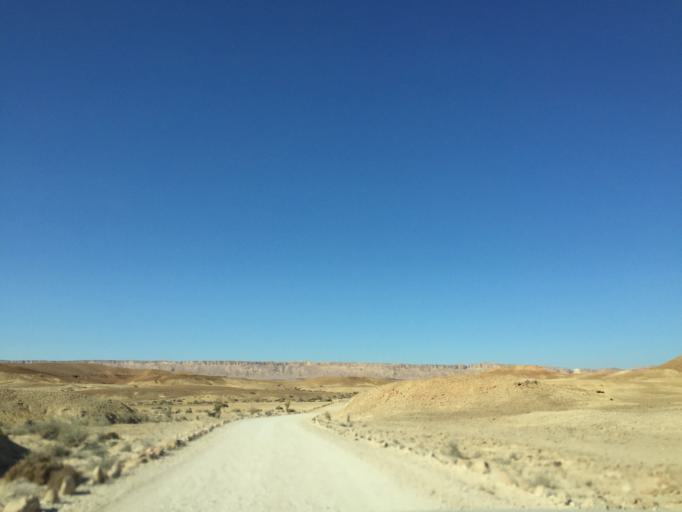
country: IL
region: Southern District
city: Mitzpe Ramon
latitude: 30.6147
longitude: 34.9321
